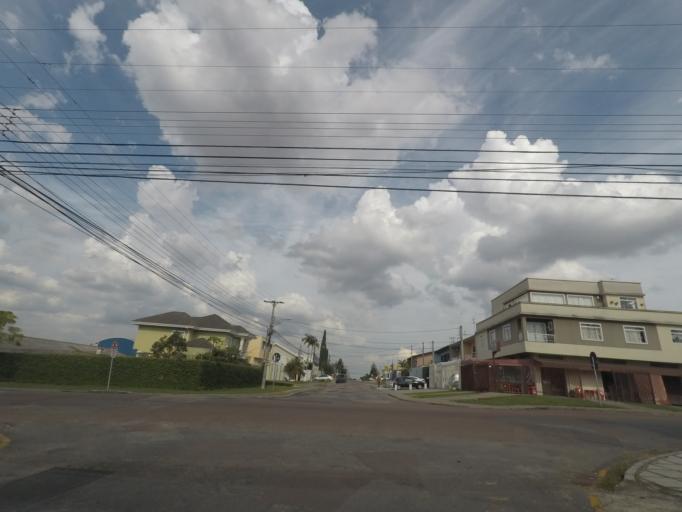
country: BR
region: Parana
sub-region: Curitiba
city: Curitiba
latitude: -25.4856
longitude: -49.2592
